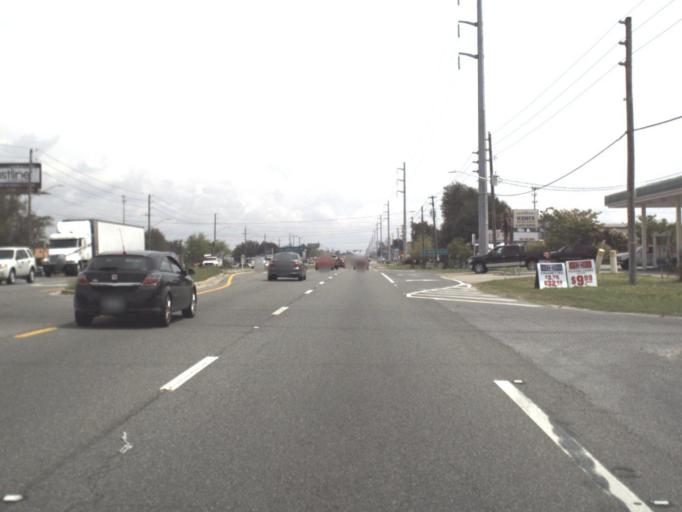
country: US
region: Florida
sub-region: Santa Rosa County
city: Oriole Beach
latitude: 30.3846
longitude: -87.1013
